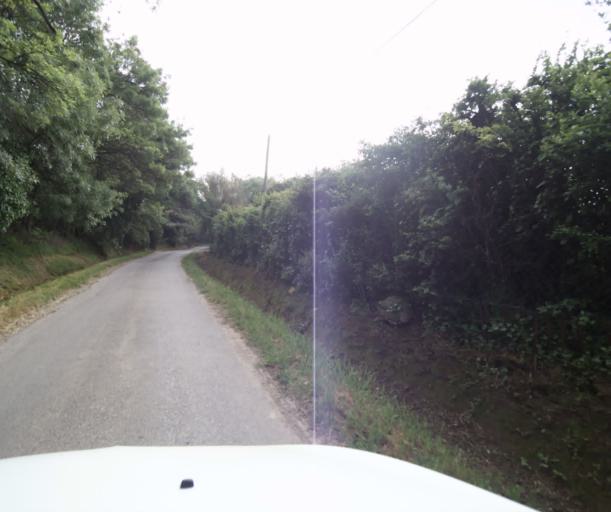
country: FR
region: Provence-Alpes-Cote d'Azur
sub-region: Departement du Var
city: Hyeres
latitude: 43.1127
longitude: 6.1548
